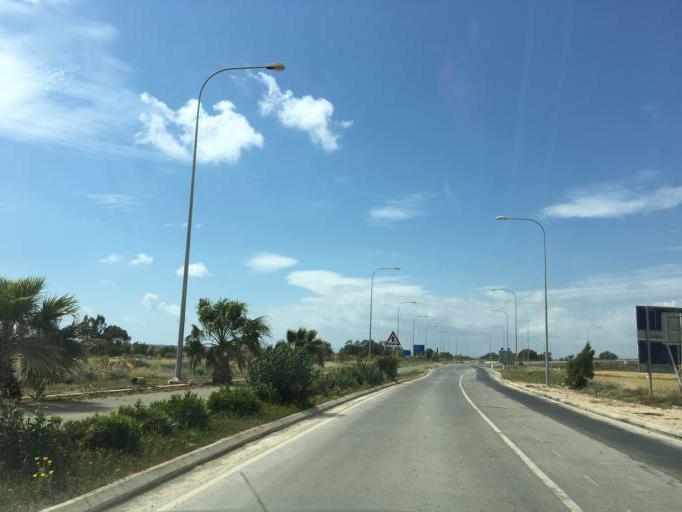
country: CY
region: Ammochostos
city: Liopetri
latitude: 34.9760
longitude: 33.8981
